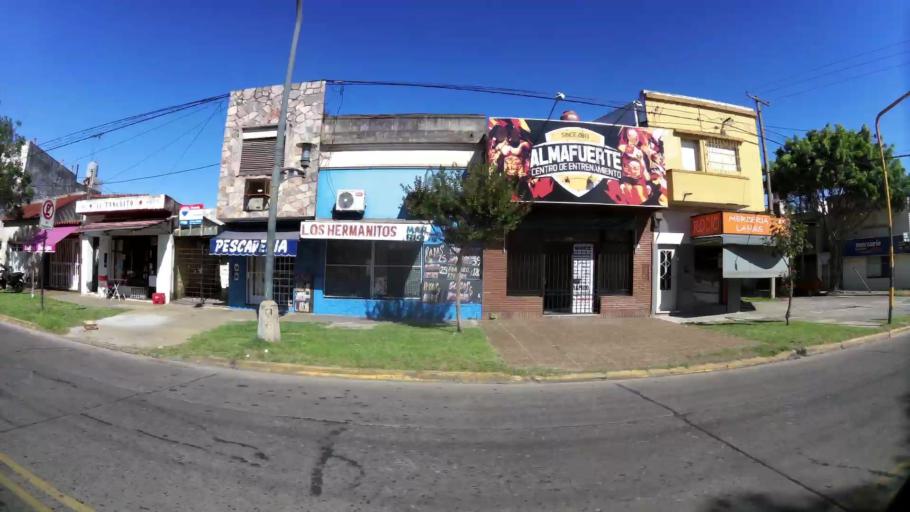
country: AR
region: Santa Fe
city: Santa Fe de la Vera Cruz
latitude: -31.6257
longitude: -60.6897
